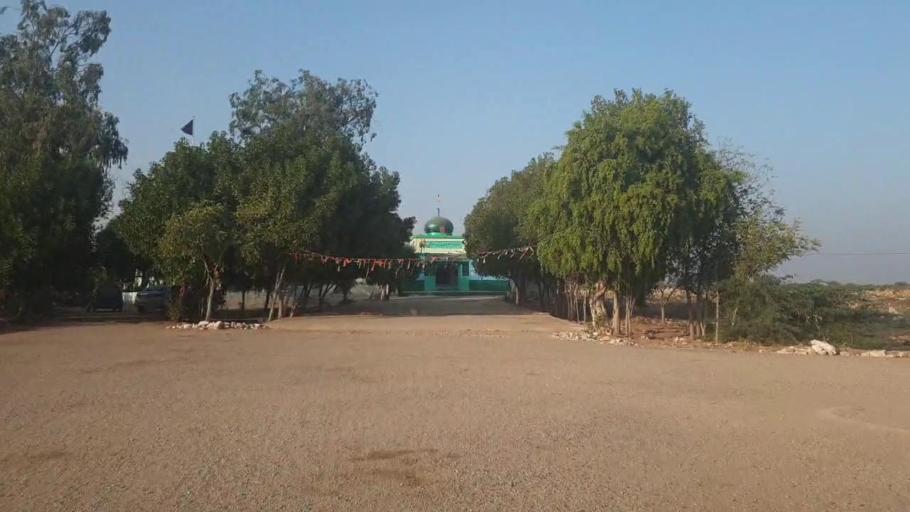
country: PK
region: Sindh
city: Jamshoro
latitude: 25.4428
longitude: 68.2894
